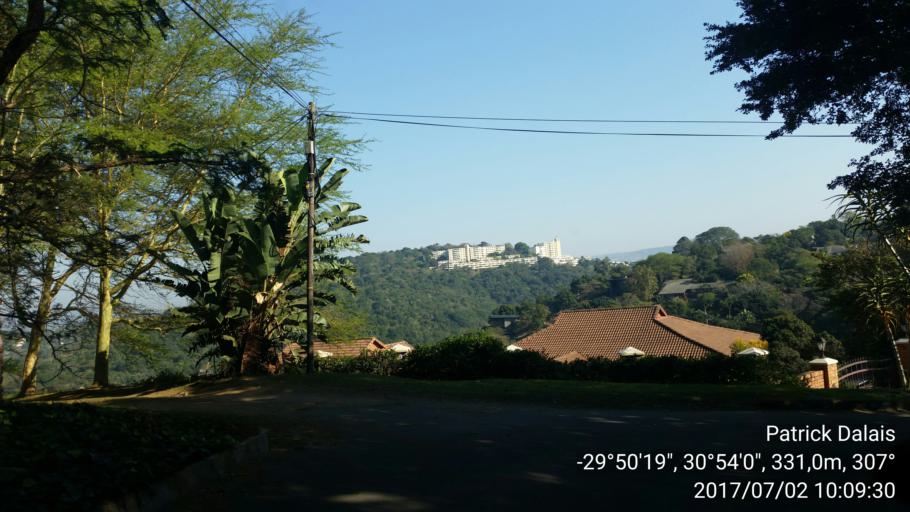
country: ZA
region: KwaZulu-Natal
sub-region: eThekwini Metropolitan Municipality
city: Berea
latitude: -29.8387
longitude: 30.9001
